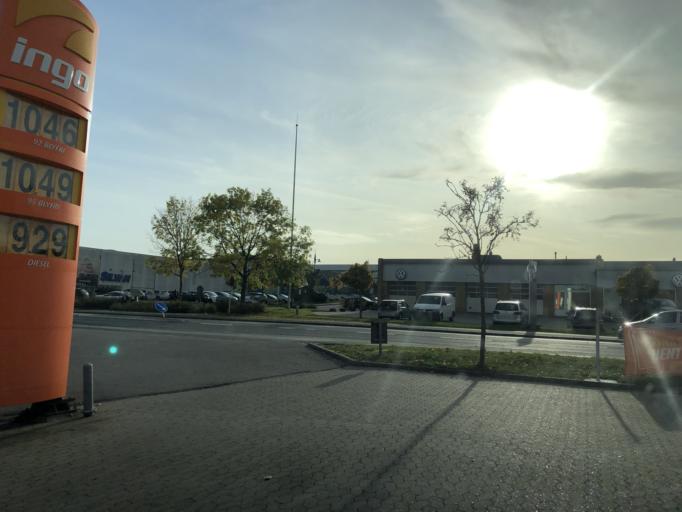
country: DK
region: Capital Region
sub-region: Rudersdal Kommune
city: Birkerod
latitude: 55.8411
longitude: 12.4405
